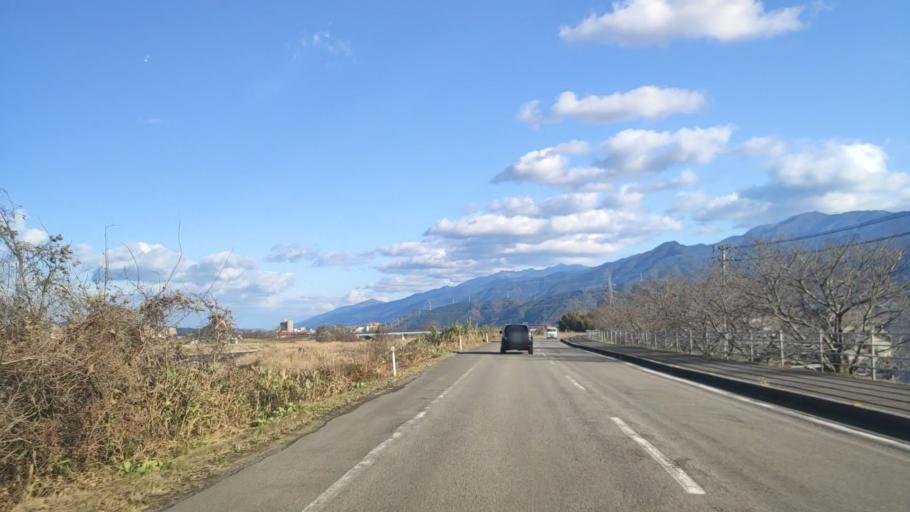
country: JP
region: Ehime
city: Saijo
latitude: 33.9108
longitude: 133.1647
